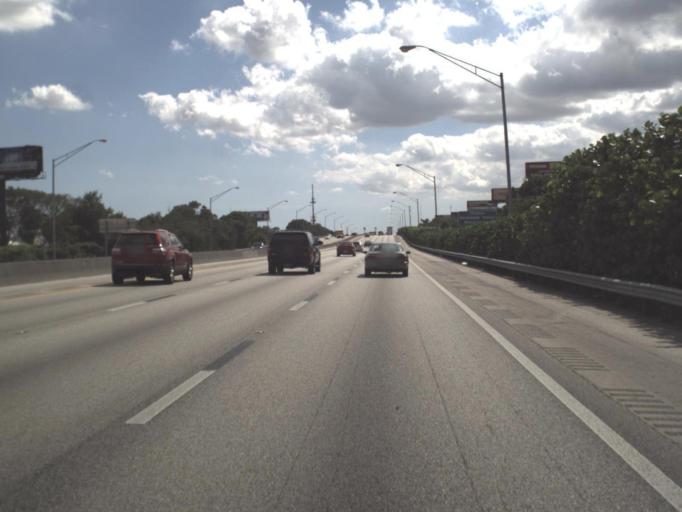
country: US
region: Florida
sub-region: Broward County
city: Davie
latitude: 26.0444
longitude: -80.2146
